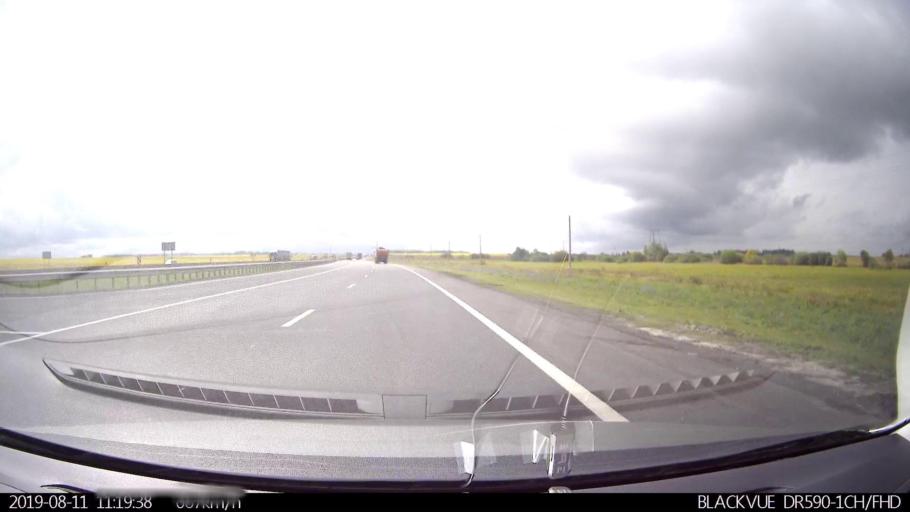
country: RU
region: Ulyanovsk
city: Novoul'yanovsk
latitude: 54.1666
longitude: 48.2647
